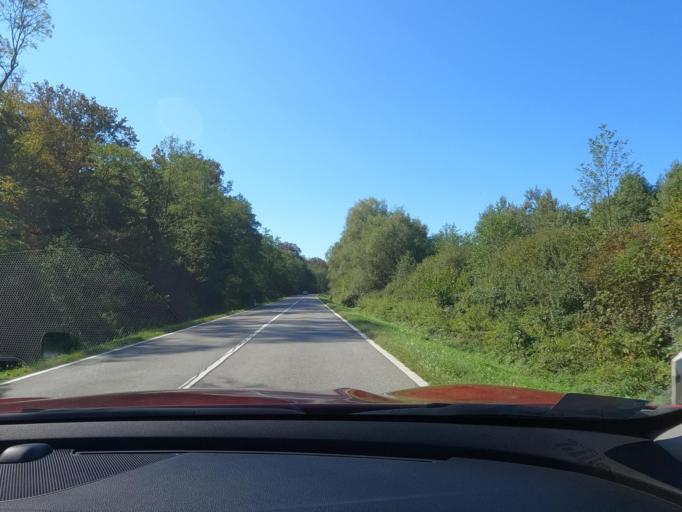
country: HR
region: Sisacko-Moslavacka
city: Osekovo
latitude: 45.5150
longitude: 16.5303
